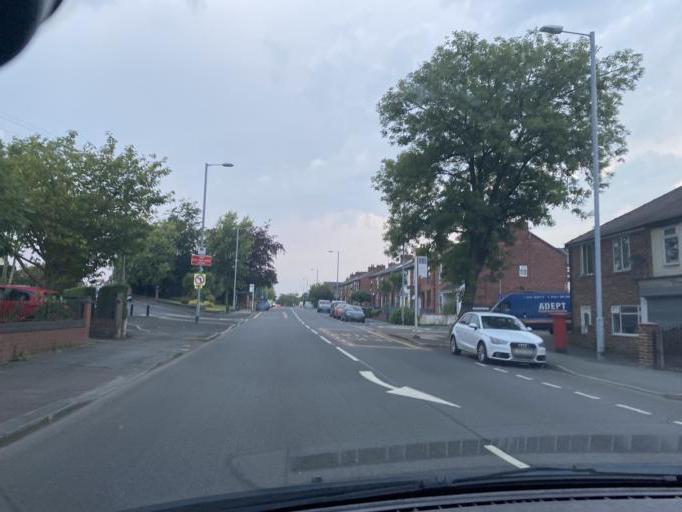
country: GB
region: England
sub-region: Borough of Tameside
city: Droylsden
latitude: 53.4737
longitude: -2.1372
